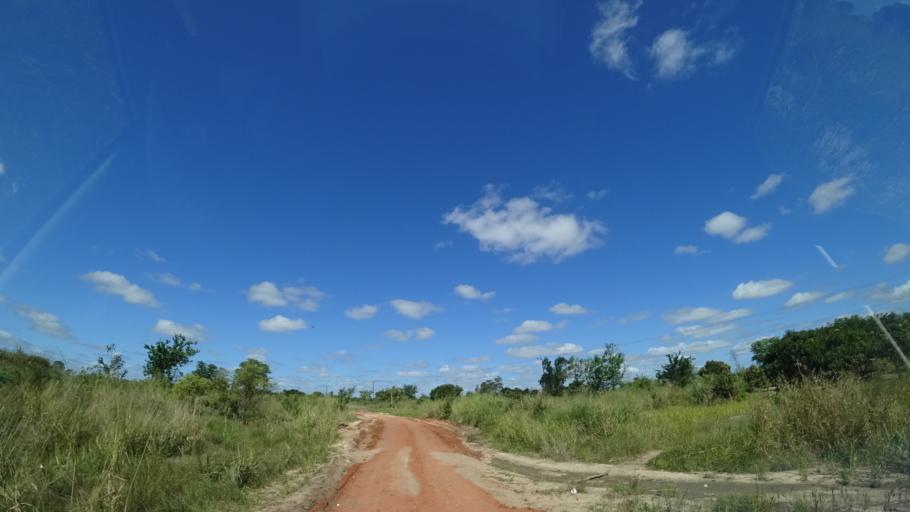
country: MZ
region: Sofala
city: Dondo
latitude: -19.2752
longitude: 34.6807
